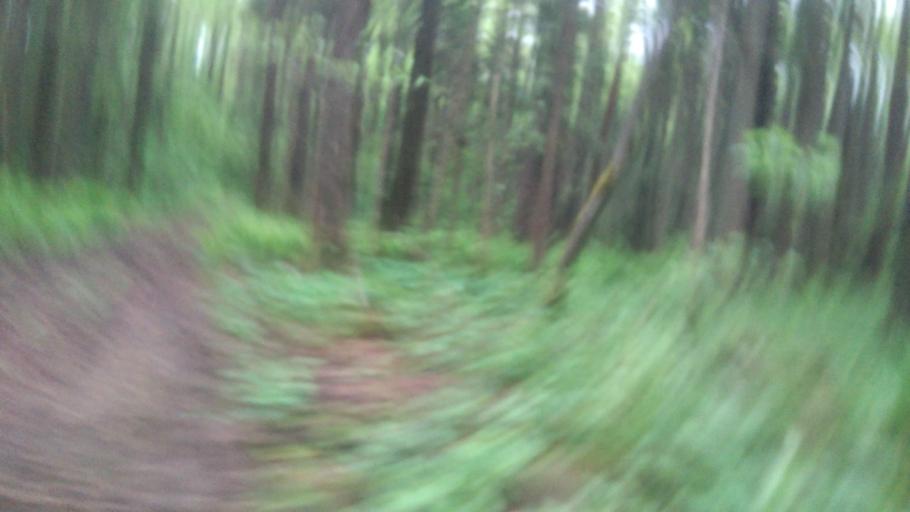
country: RU
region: Perm
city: Froly
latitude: 57.9593
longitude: 56.3137
